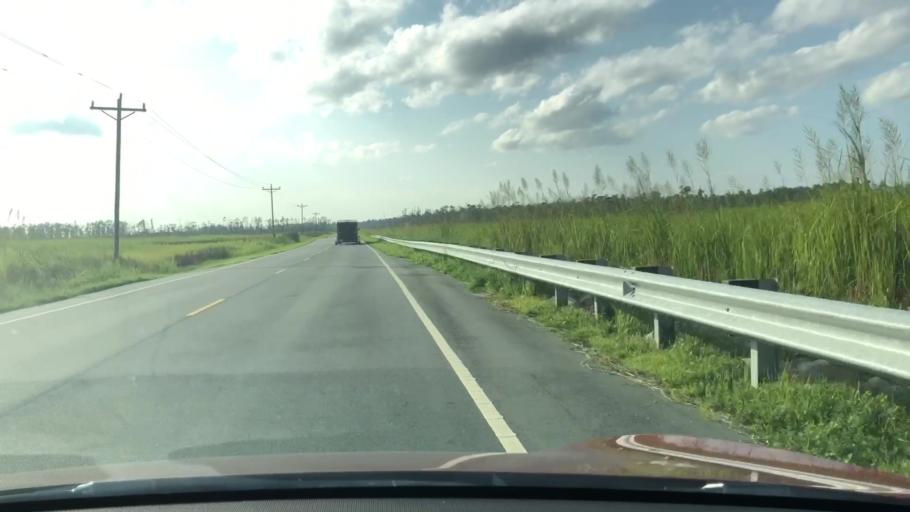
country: US
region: North Carolina
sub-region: Dare County
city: Wanchese
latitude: 35.6321
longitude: -75.8558
